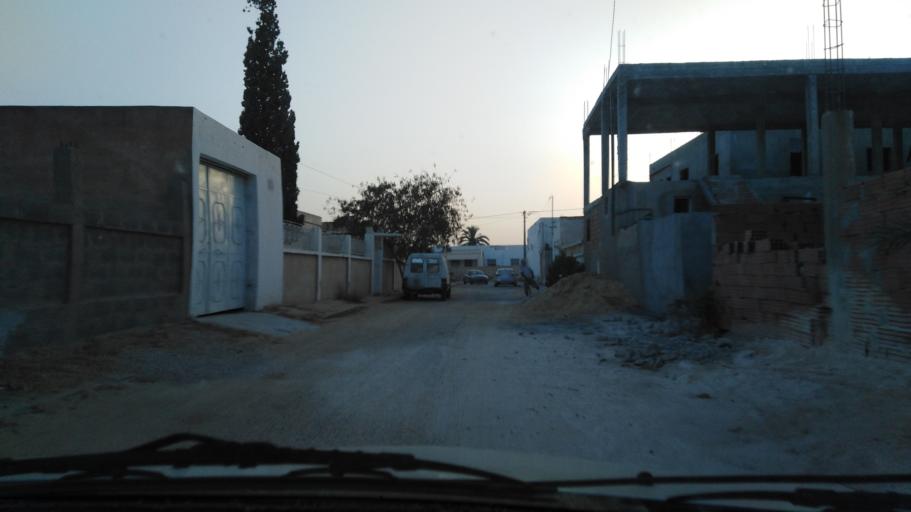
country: TN
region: Qabis
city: Gabes
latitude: 33.9545
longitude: 9.9984
